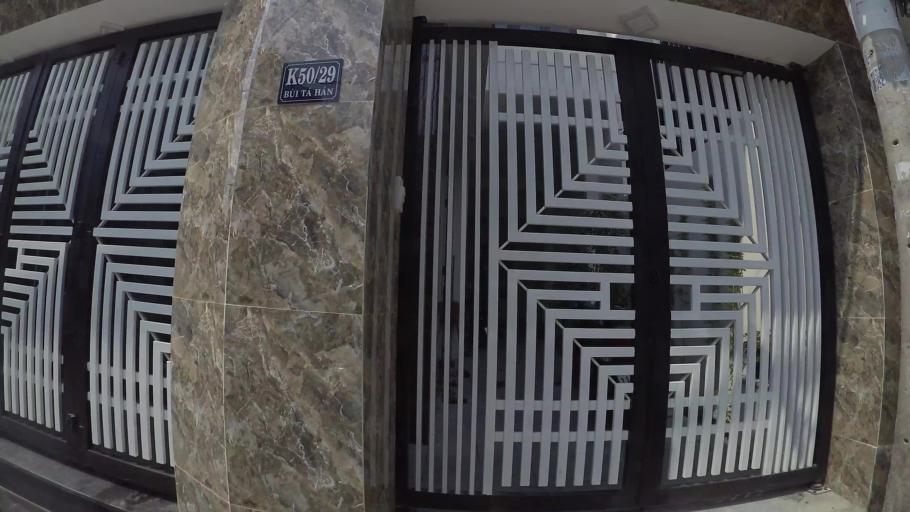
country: VN
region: Da Nang
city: Ngu Hanh Son
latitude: 16.0322
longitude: 108.2442
